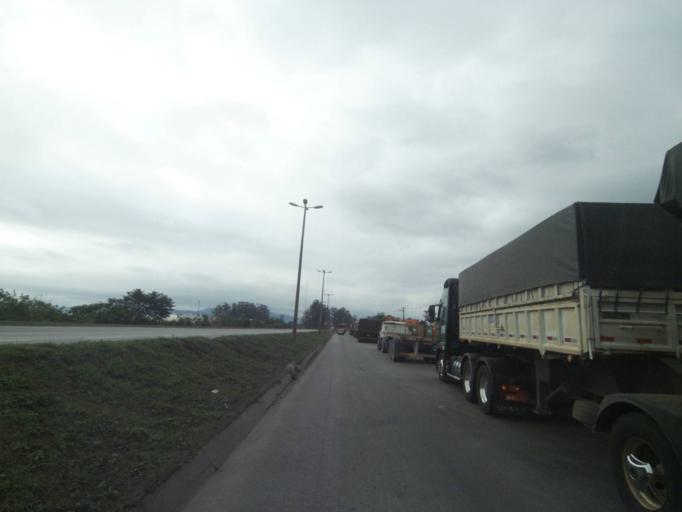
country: BR
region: Parana
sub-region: Paranagua
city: Paranagua
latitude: -25.5438
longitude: -48.5594
